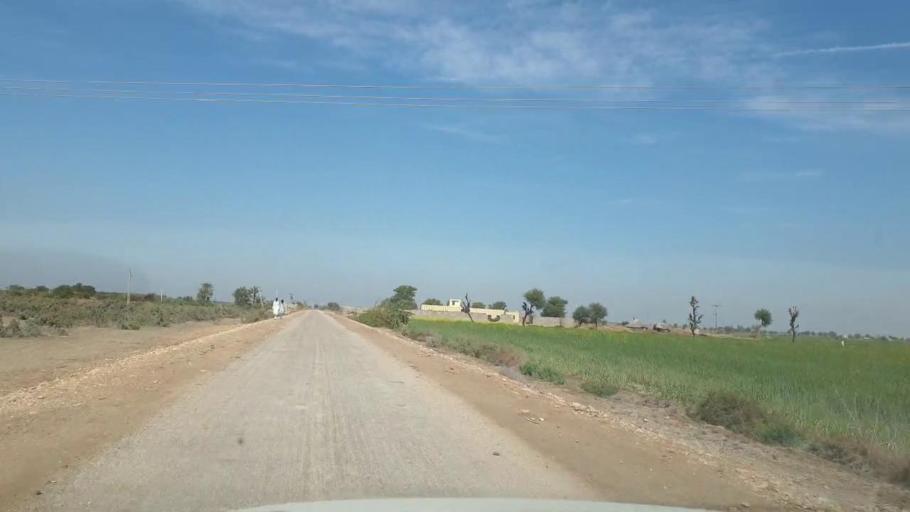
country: PK
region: Sindh
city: Mirpur Khas
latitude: 25.6329
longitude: 69.1967
